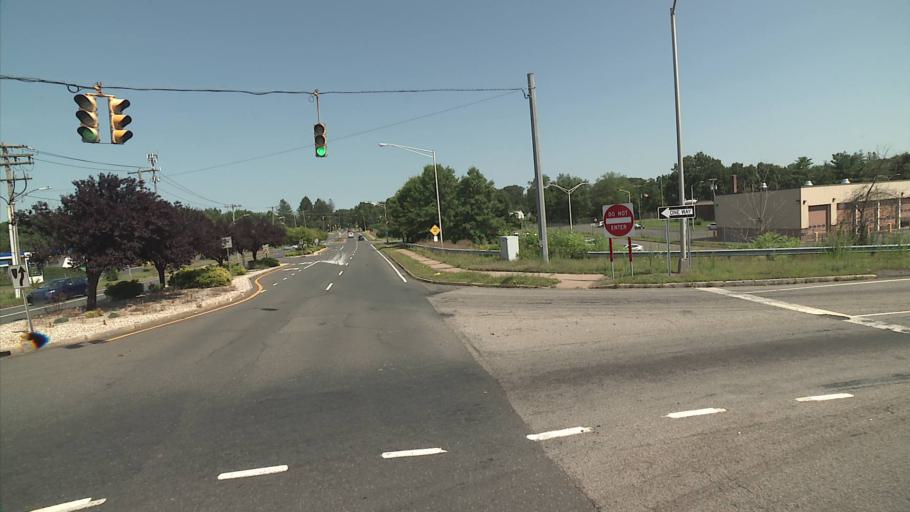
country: US
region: Connecticut
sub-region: Hartford County
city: Windsor
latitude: 41.8521
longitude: -72.6634
